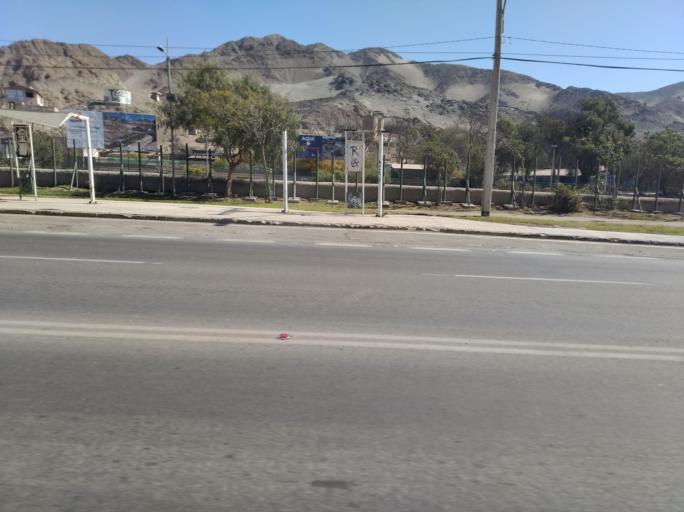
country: CL
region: Atacama
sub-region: Provincia de Copiapo
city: Copiapo
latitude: -27.3663
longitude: -70.3400
